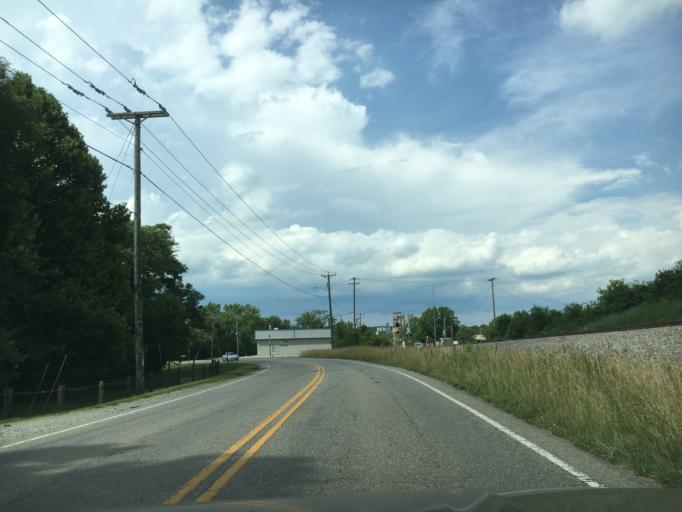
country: US
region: Virginia
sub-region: Roanoke County
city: Cave Spring
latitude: 37.1998
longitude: -79.9988
